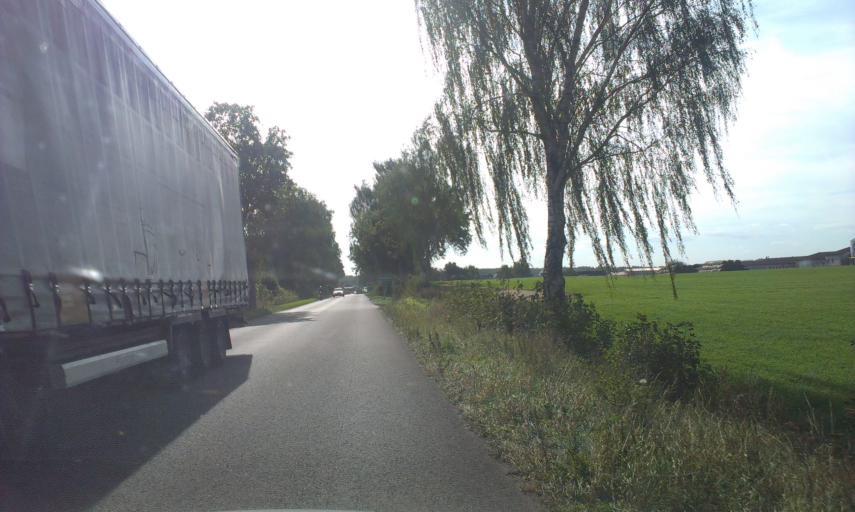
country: PL
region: Greater Poland Voivodeship
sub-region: Powiat zlotowski
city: Zlotow
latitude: 53.4502
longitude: 16.9860
